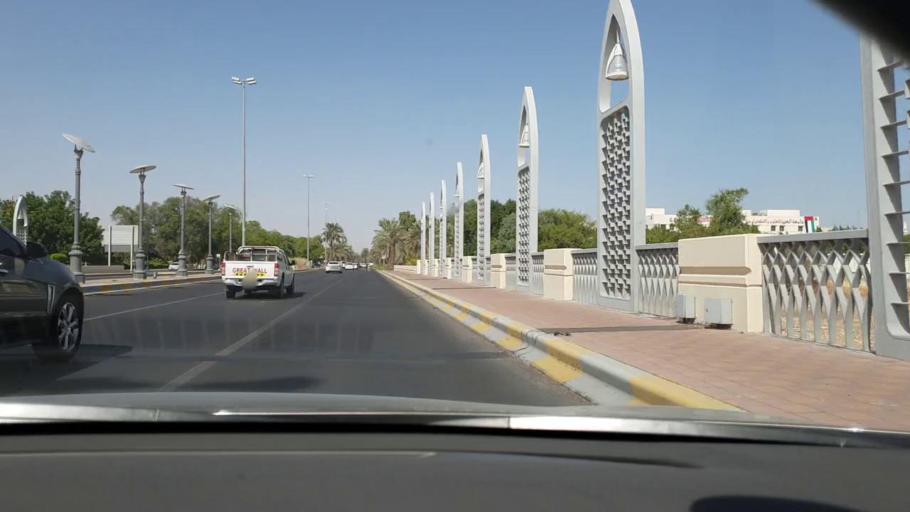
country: AE
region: Abu Dhabi
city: Al Ain
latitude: 24.2366
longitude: 55.7388
